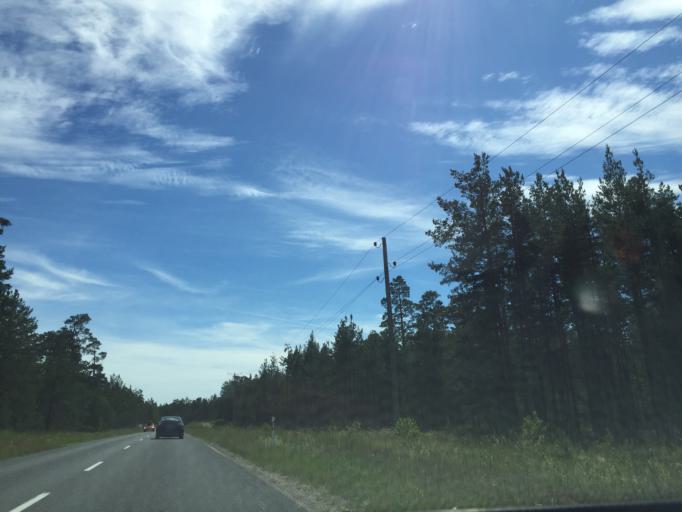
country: LV
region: Dundaga
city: Dundaga
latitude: 57.6475
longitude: 22.5717
